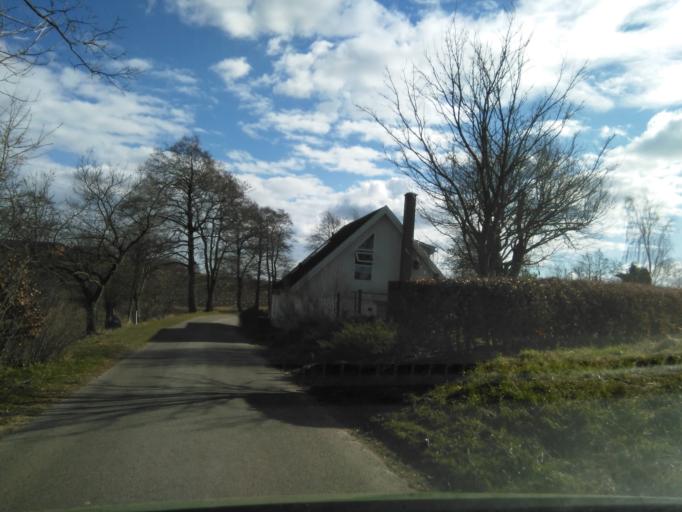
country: DK
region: Central Jutland
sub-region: Odder Kommune
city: Odder
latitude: 55.9126
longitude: 10.0355
